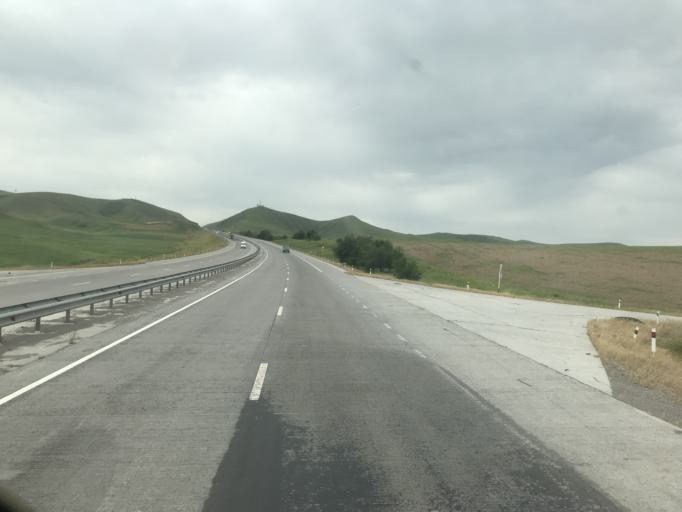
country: KZ
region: Ongtustik Qazaqstan
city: Qazyqurt
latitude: 42.0219
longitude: 69.4695
